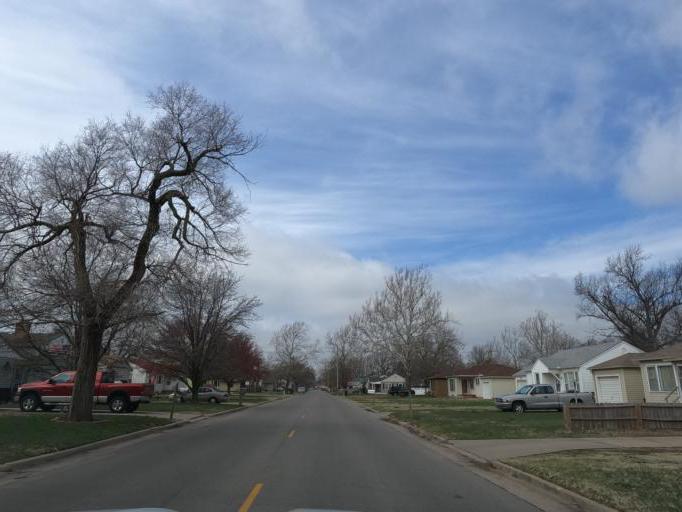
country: US
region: Kansas
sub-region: Reno County
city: Hutchinson
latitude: 38.0810
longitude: -97.9344
